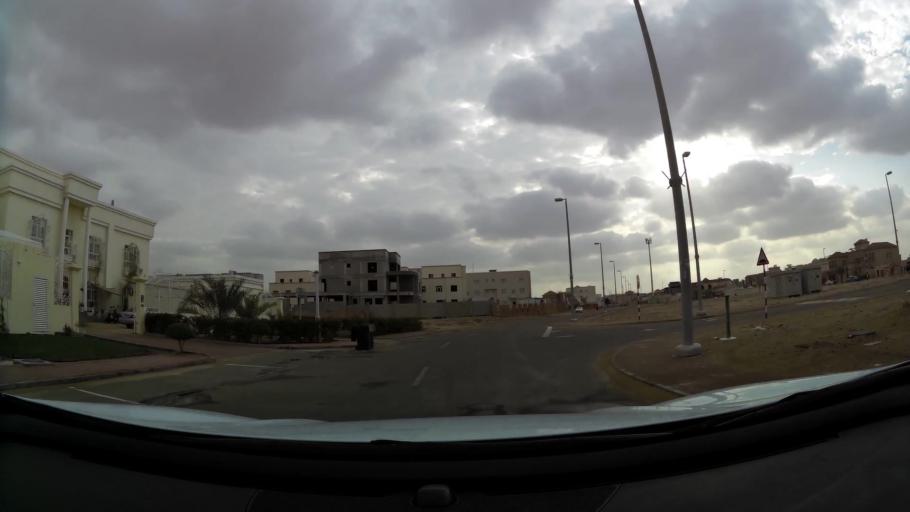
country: AE
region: Abu Dhabi
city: Abu Dhabi
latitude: 24.3528
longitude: 54.6128
